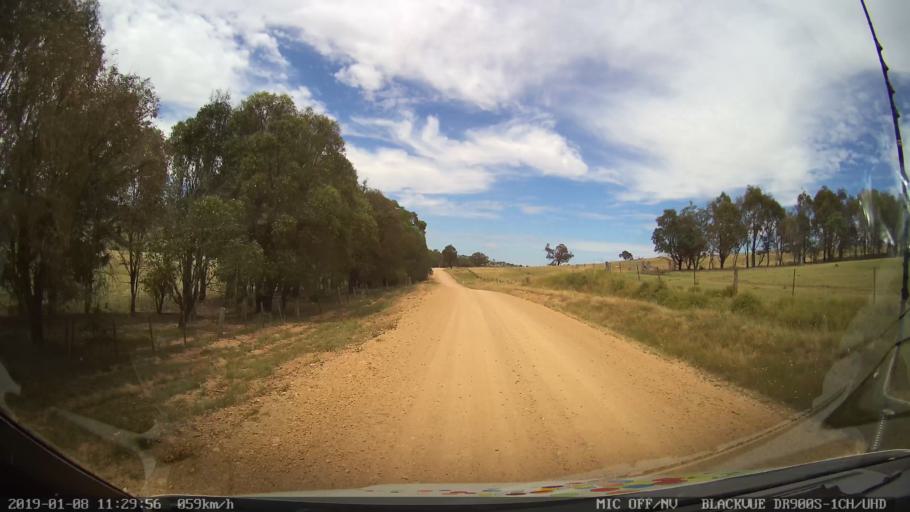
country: AU
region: New South Wales
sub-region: Guyra
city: Guyra
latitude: -30.3040
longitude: 151.5466
